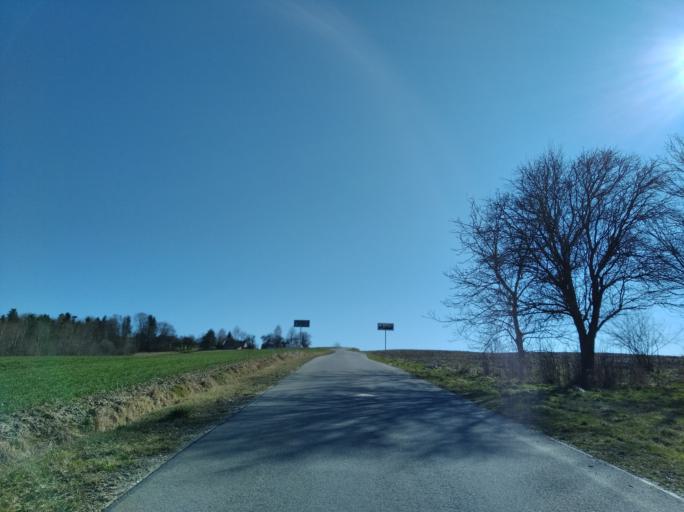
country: PL
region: Subcarpathian Voivodeship
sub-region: Powiat strzyzowski
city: Wisniowa
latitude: 49.9104
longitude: 21.6976
